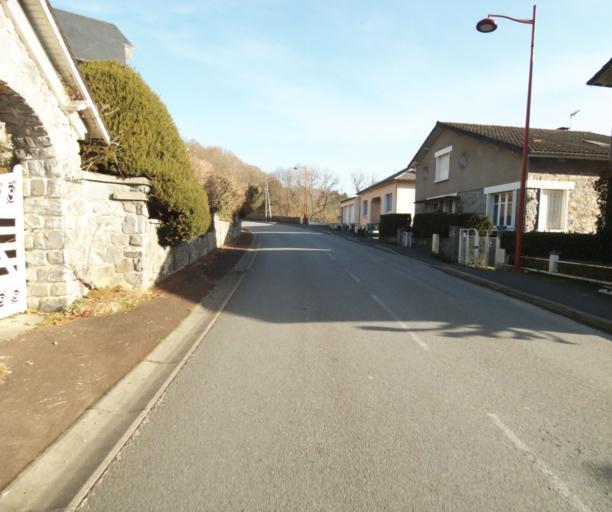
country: FR
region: Limousin
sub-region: Departement de la Correze
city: Laguenne
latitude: 45.2462
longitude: 1.7774
